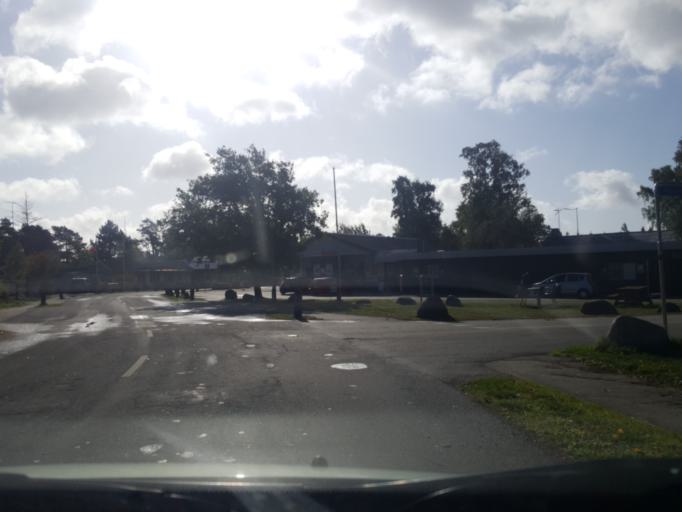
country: DK
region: Zealand
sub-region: Guldborgsund Kommune
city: Nykobing Falster
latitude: 54.6697
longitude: 11.9560
